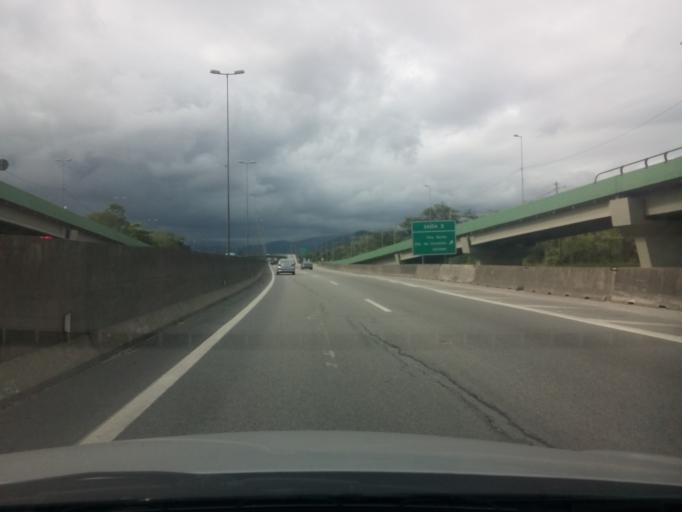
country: BR
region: Sao Paulo
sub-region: Santos
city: Santos
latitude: -23.9415
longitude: -46.2803
